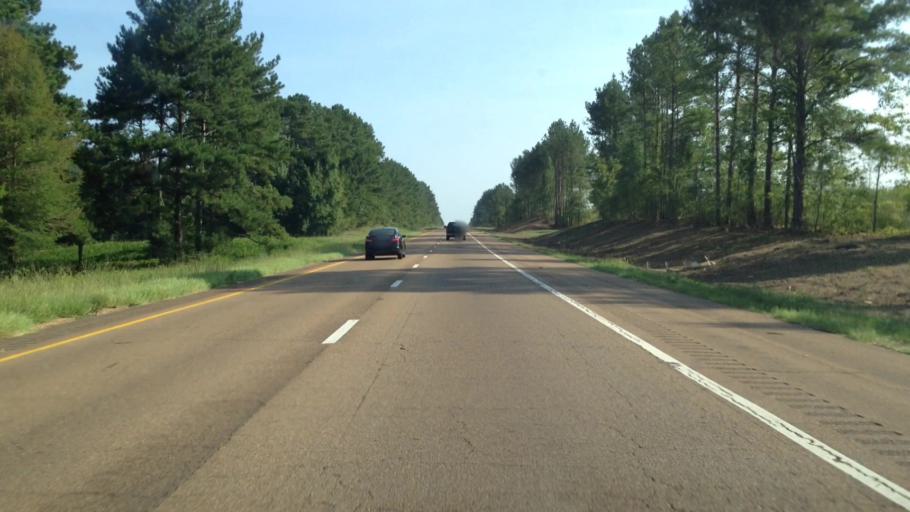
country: US
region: Mississippi
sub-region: Lincoln County
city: Brookhaven
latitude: 31.4586
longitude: -90.4789
